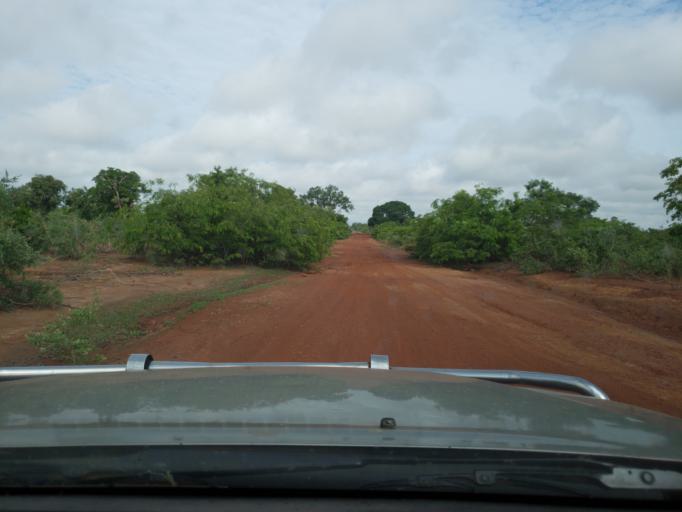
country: ML
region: Sikasso
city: Koutiala
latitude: 12.3924
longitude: -6.0038
